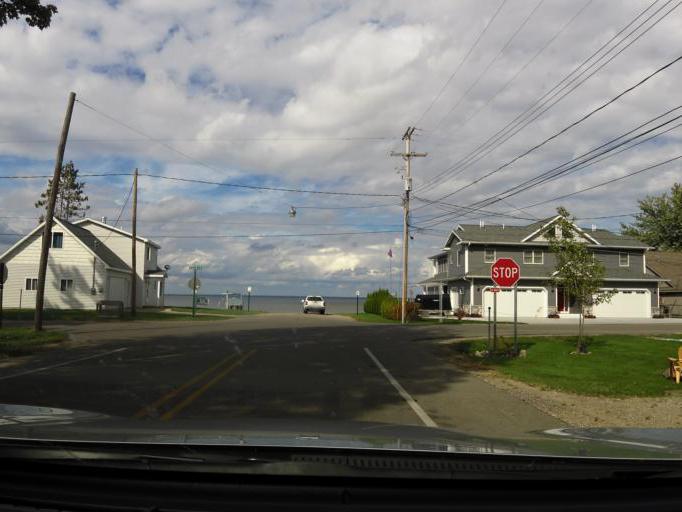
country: US
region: Michigan
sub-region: Roscommon County
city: Houghton Lake
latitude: 44.2995
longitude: -84.7123
